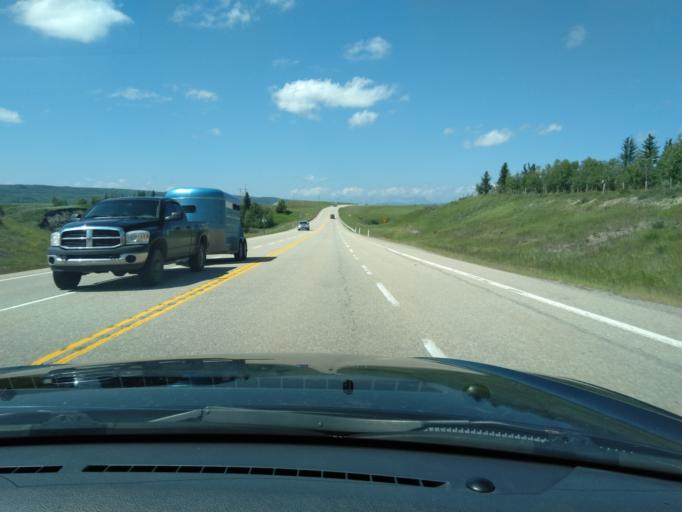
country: CA
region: Alberta
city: Cochrane
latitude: 51.2267
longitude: -114.5822
